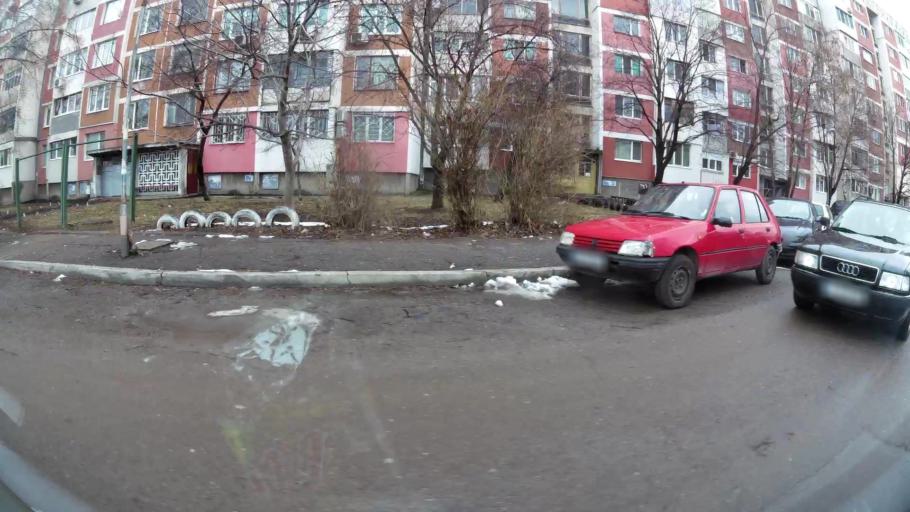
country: BG
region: Sofiya
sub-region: Obshtina Bozhurishte
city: Bozhurishte
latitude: 42.7307
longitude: 23.2487
